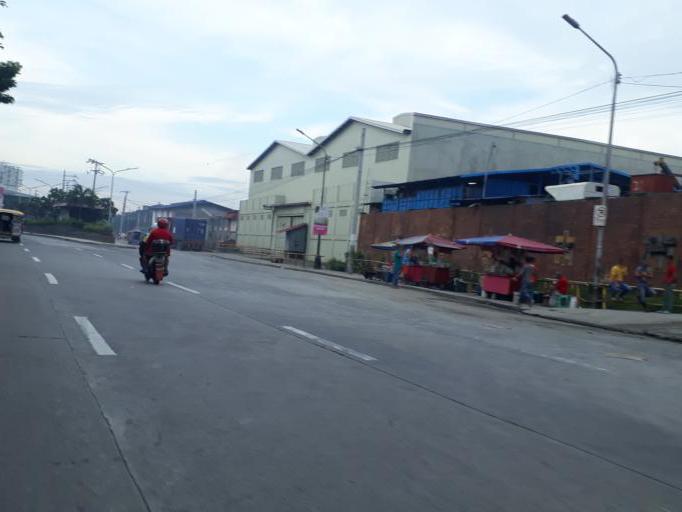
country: PH
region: Metro Manila
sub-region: Caloocan City
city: Niugan
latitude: 14.6587
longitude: 120.9660
